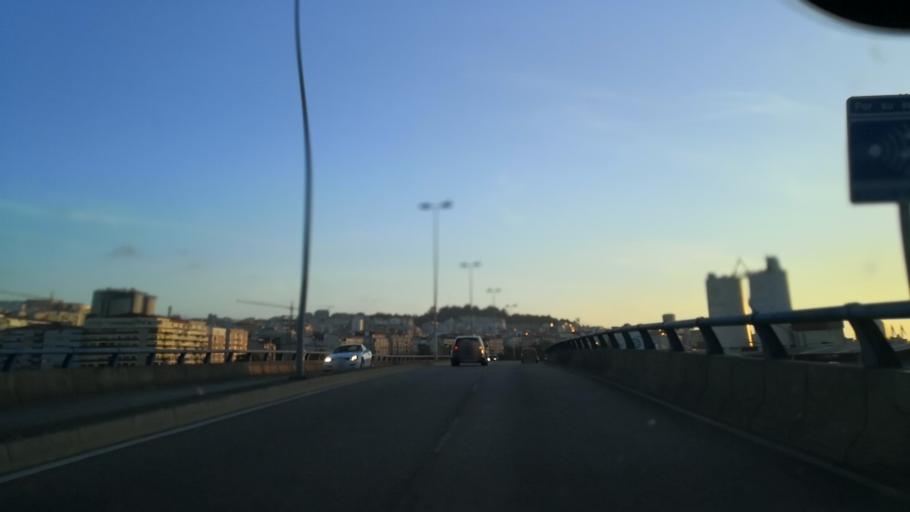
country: ES
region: Galicia
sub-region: Provincia de Pontevedra
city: Vigo
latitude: 42.2425
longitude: -8.7077
